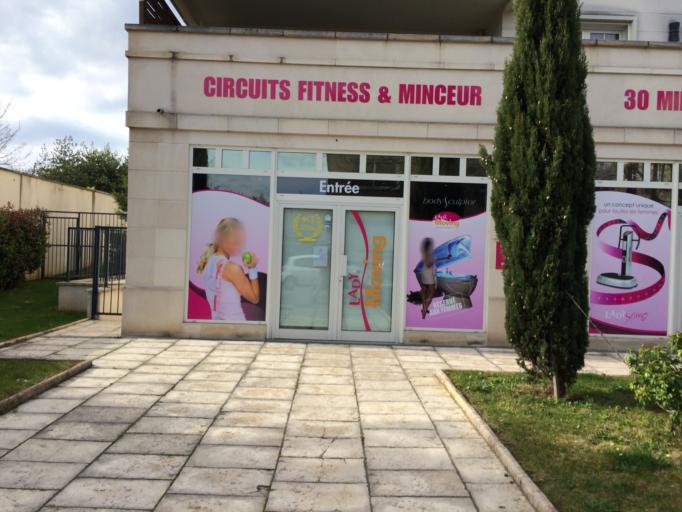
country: FR
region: Ile-de-France
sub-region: Departement du Val-de-Marne
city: Joinville-le-Pont
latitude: 48.8077
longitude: 2.4758
